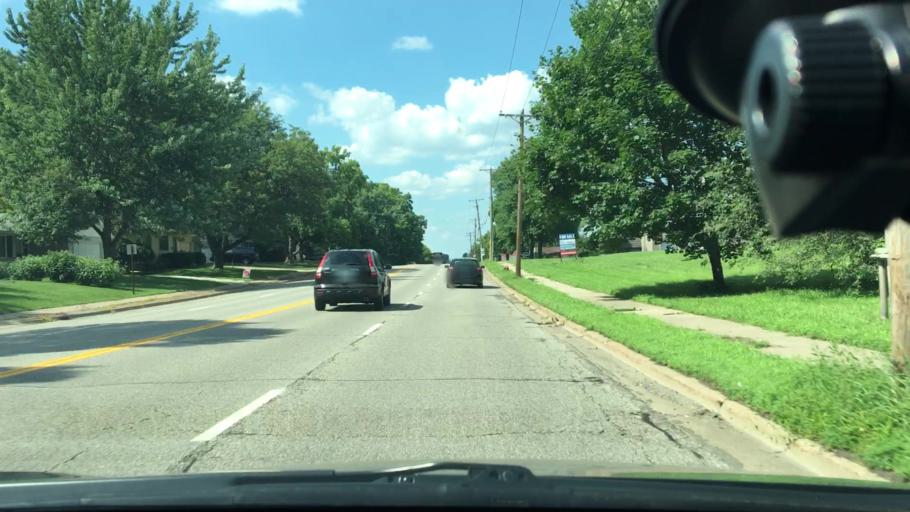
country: US
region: Minnesota
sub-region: Hennepin County
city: New Hope
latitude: 45.0161
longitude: -93.3802
